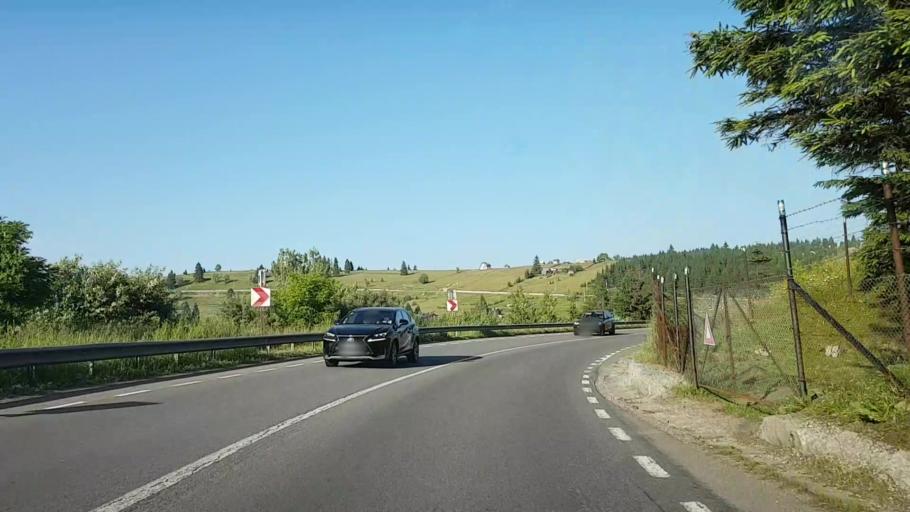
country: RO
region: Bistrita-Nasaud
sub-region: Comuna Lunca Ilvei
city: Lunca Ilvei
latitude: 47.2419
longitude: 25.0102
